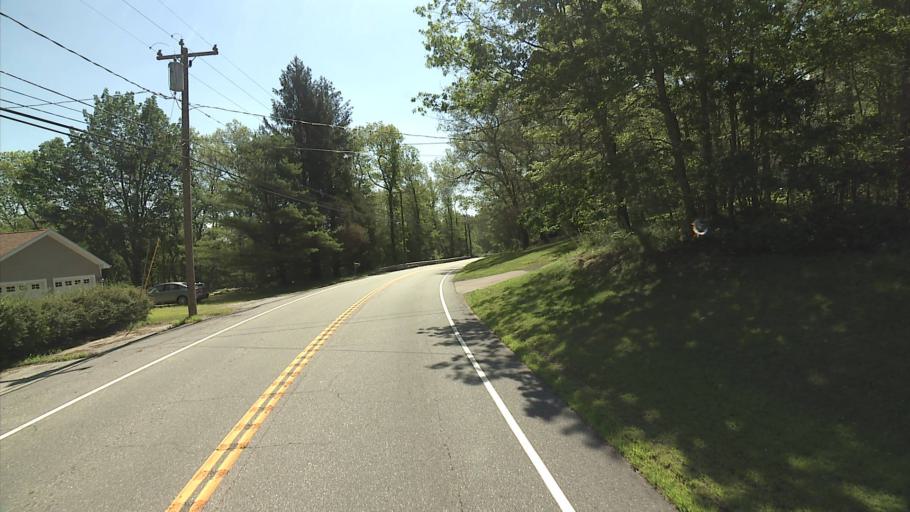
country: US
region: Connecticut
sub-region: Windham County
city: Moosup
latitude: 41.7190
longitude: -71.8506
